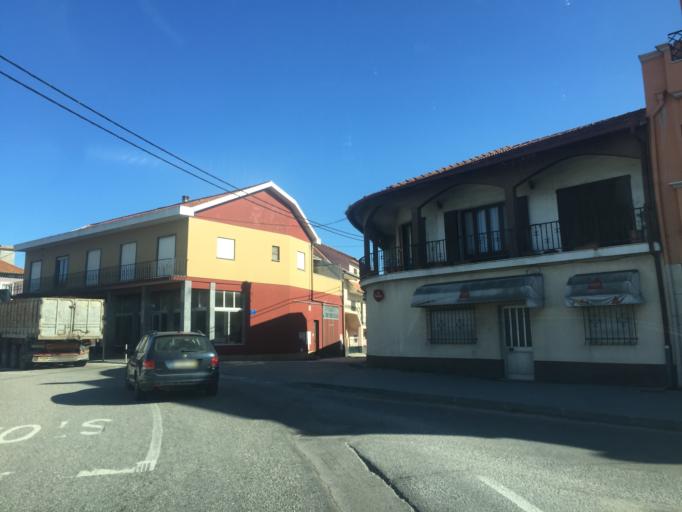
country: PT
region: Leiria
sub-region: Leiria
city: Monte Redondo
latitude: 39.9459
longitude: -8.7848
